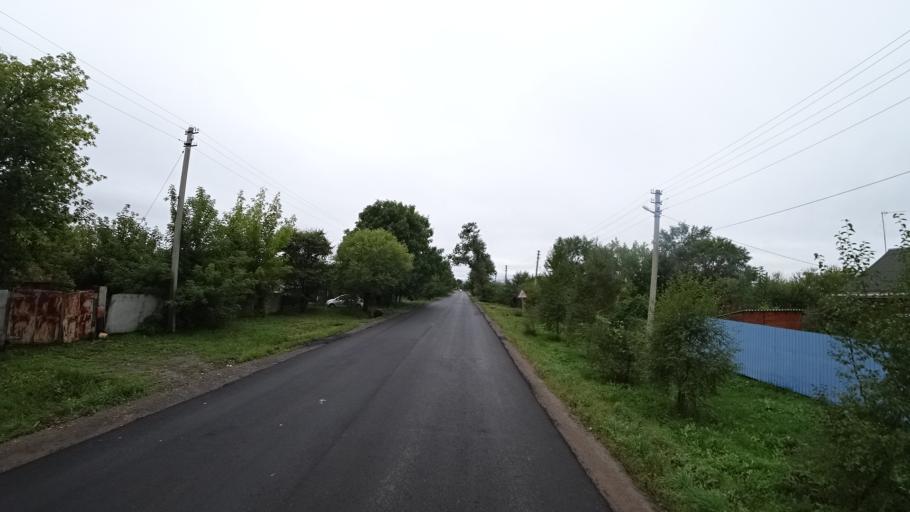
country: RU
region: Primorskiy
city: Monastyrishche
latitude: 44.1946
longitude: 132.4979
